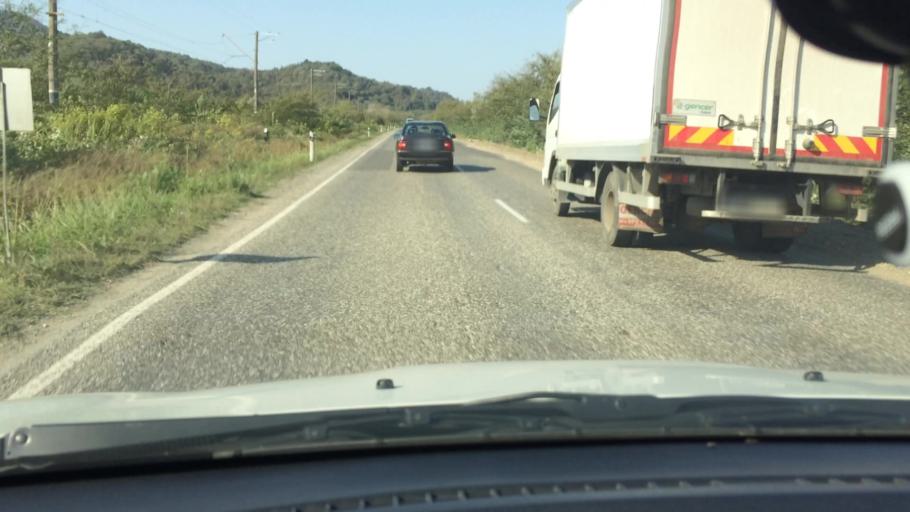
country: GE
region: Samegrelo and Zemo Svaneti
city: Abasha
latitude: 42.0957
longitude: 42.2303
